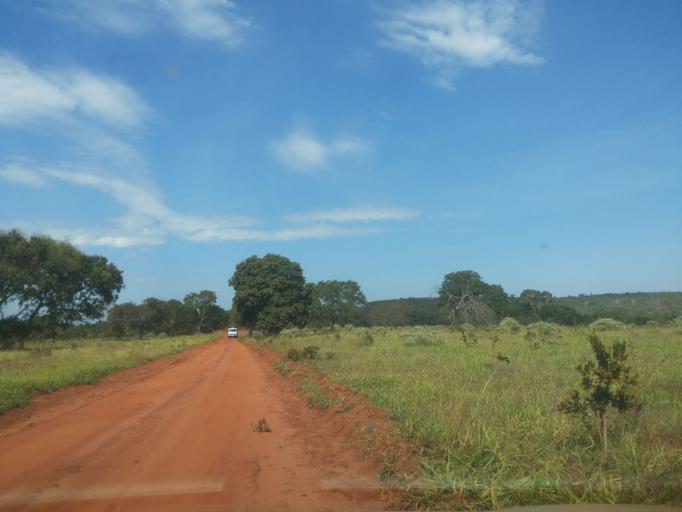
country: BR
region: Minas Gerais
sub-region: Ituiutaba
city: Ituiutaba
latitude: -19.0629
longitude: -49.3643
